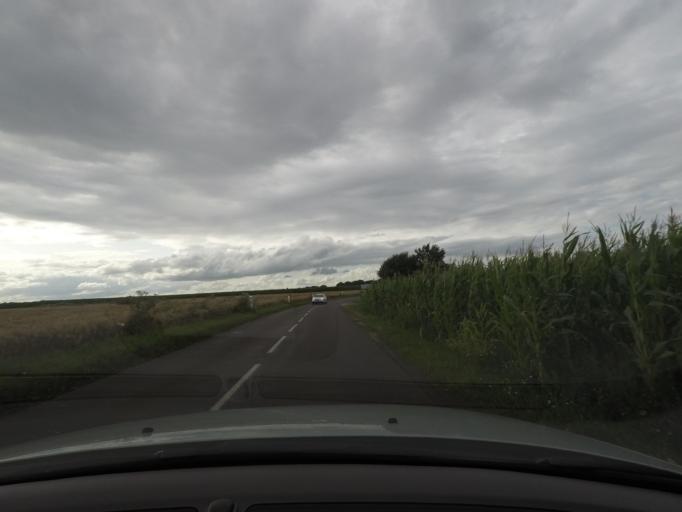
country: FR
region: Haute-Normandie
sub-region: Departement de la Seine-Maritime
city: Ymare
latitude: 49.3417
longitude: 1.1871
